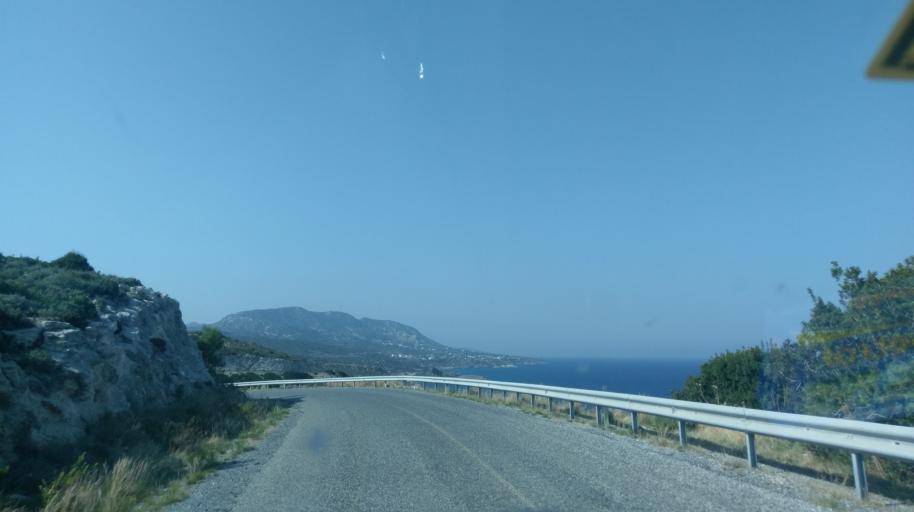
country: CY
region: Keryneia
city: Lapithos
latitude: 35.3541
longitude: 33.0750
